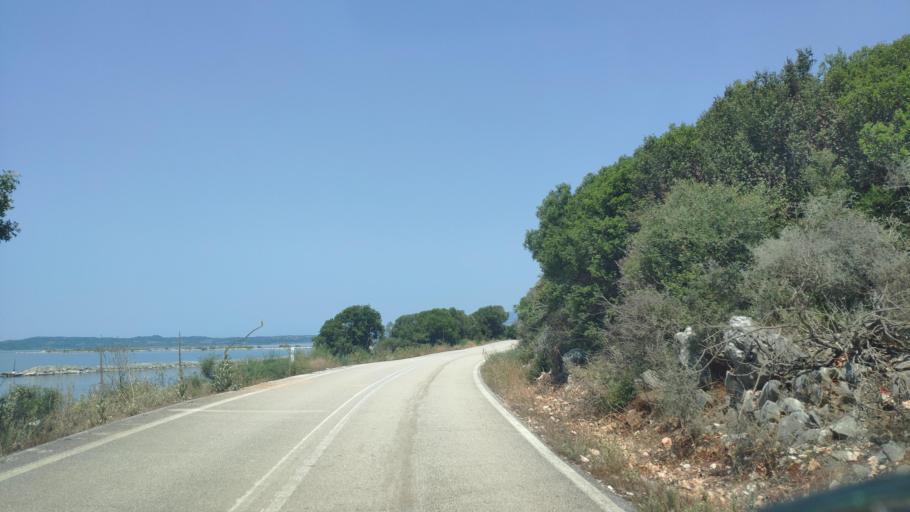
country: GR
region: Epirus
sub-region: Nomos Artas
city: Aneza
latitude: 39.0317
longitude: 20.8630
